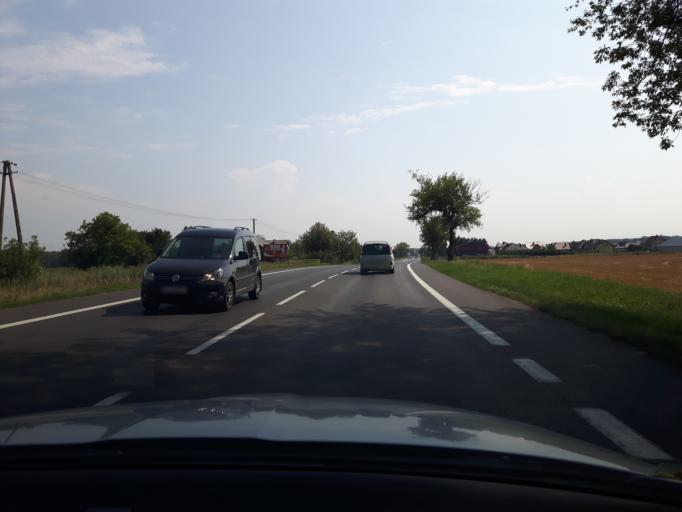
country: PL
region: Masovian Voivodeship
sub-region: Powiat mlawski
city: Strzegowo
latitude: 52.9030
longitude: 20.2870
